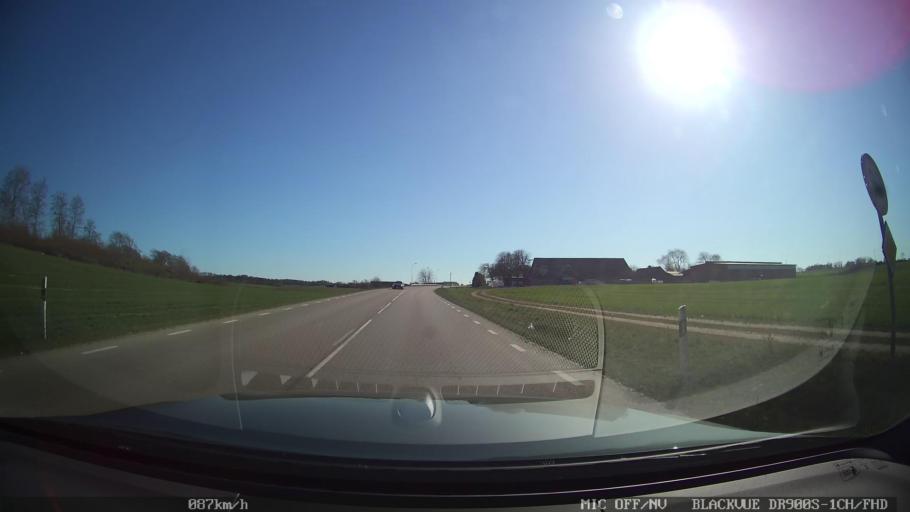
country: SE
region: Skane
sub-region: Klippans Kommun
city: Ljungbyhed
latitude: 55.9685
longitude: 13.2585
